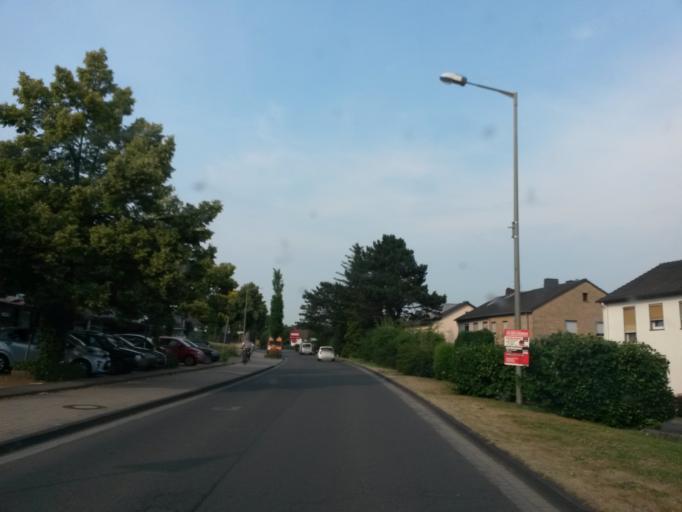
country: DE
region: North Rhine-Westphalia
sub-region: Regierungsbezirk Koln
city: Hennef
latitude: 50.8446
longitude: 7.3383
